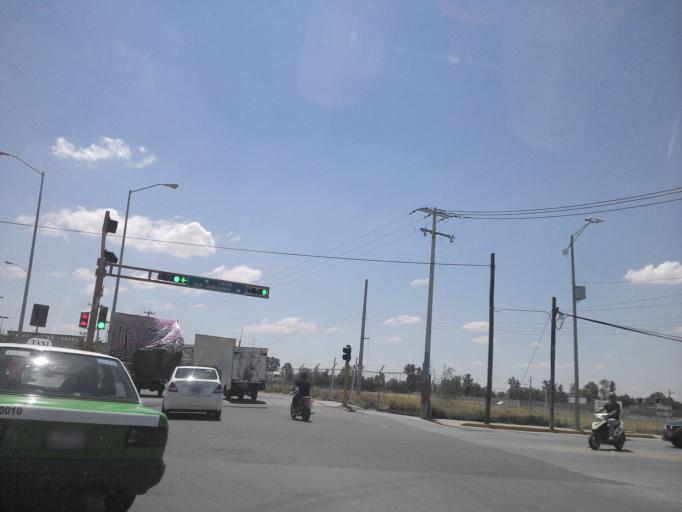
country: MX
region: Guanajuato
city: San Francisco del Rincon
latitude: 21.0247
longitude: -101.8744
